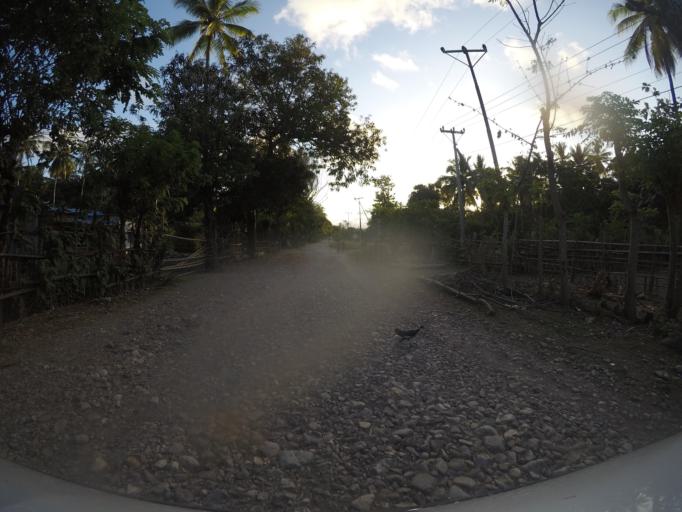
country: TL
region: Baucau
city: Venilale
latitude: -8.7462
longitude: 126.7126
